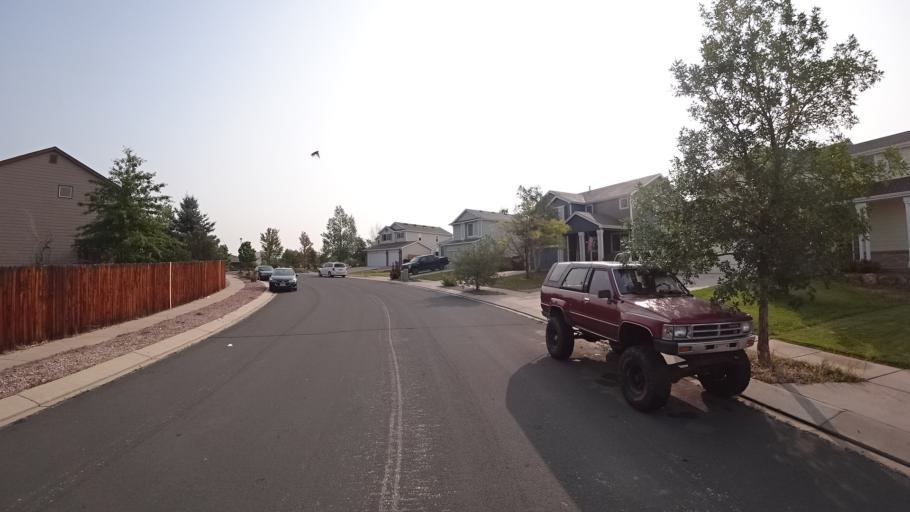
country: US
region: Colorado
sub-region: El Paso County
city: Cimarron Hills
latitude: 38.9318
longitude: -104.7312
